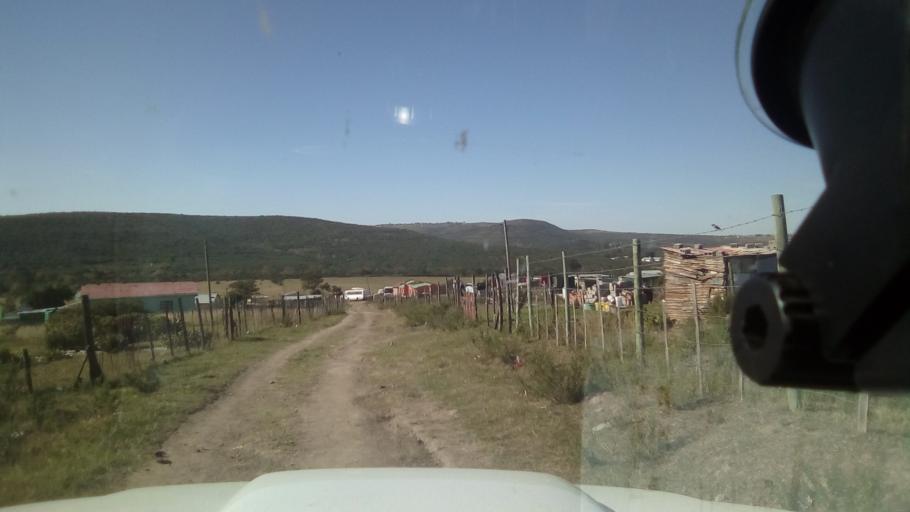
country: ZA
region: Eastern Cape
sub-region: Buffalo City Metropolitan Municipality
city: Bhisho
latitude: -32.8089
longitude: 27.3677
